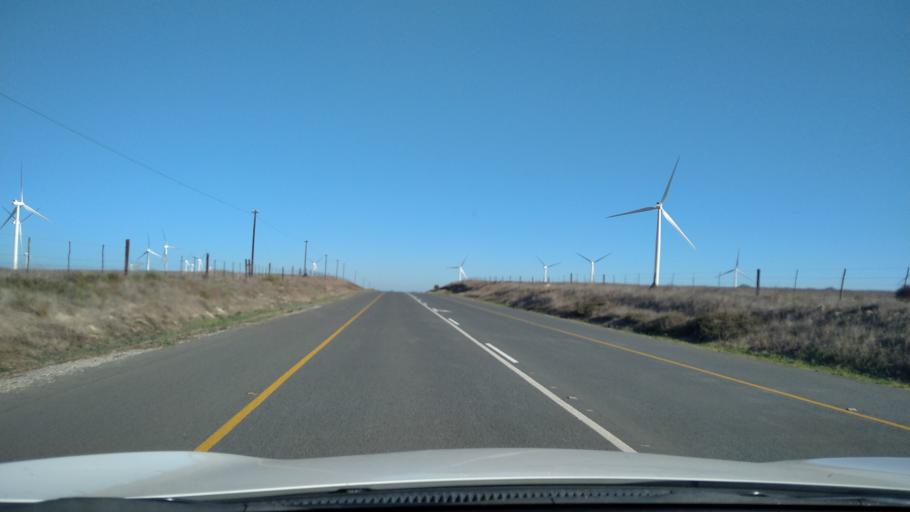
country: ZA
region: Western Cape
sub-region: West Coast District Municipality
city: Moorreesburg
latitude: -33.0957
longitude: 18.4154
